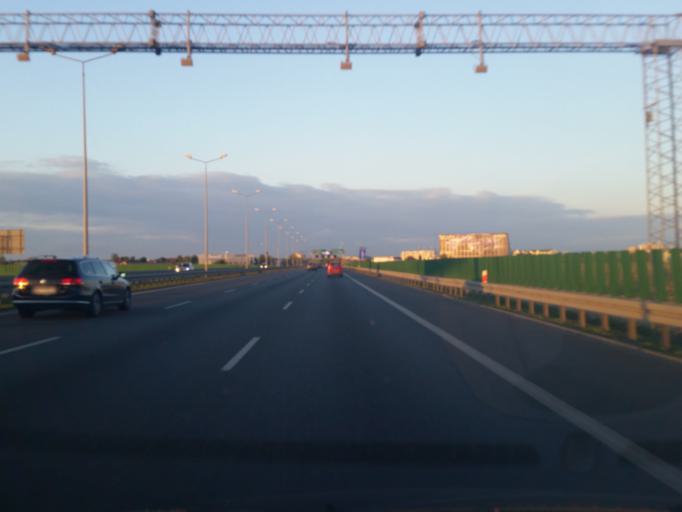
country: PL
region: Masovian Voivodeship
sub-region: Warszawa
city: Bemowo
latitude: 52.2338
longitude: 20.8824
